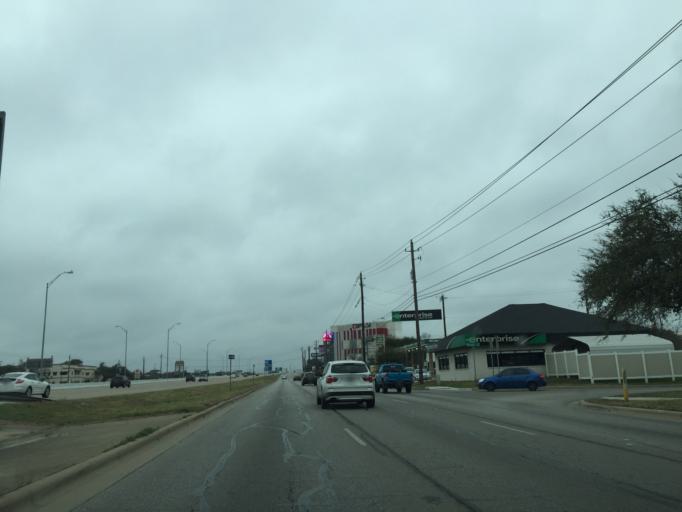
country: US
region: Texas
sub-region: Williamson County
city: Jollyville
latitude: 30.4422
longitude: -97.7828
